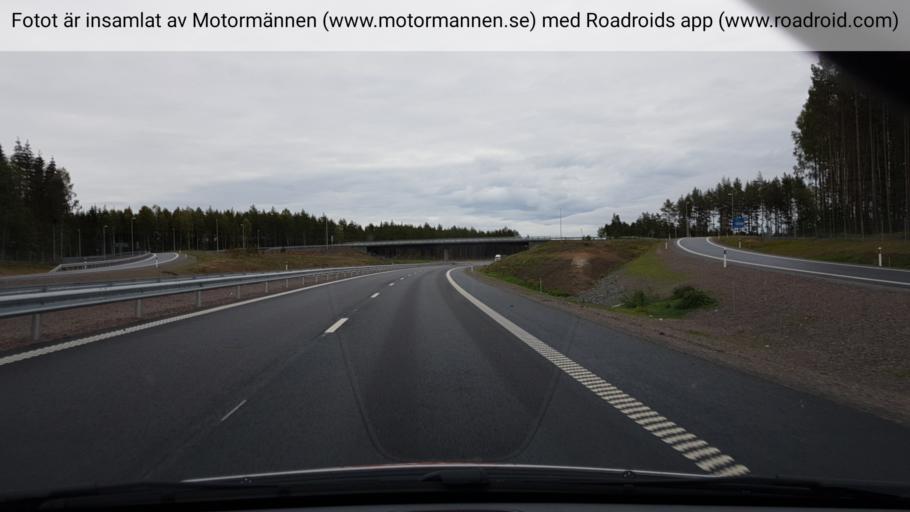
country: SE
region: Vaermland
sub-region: Karlstads Kommun
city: Edsvalla
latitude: 59.3925
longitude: 13.2798
